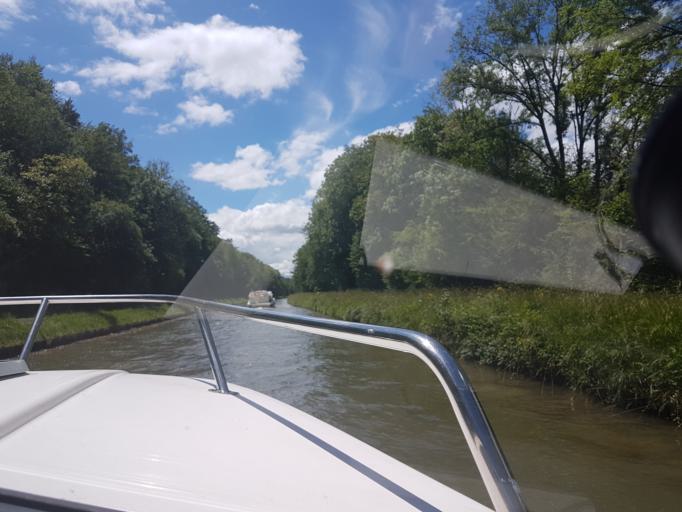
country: FR
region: Bourgogne
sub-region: Departement de l'Yonne
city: Vermenton
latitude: 47.5947
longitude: 3.6703
